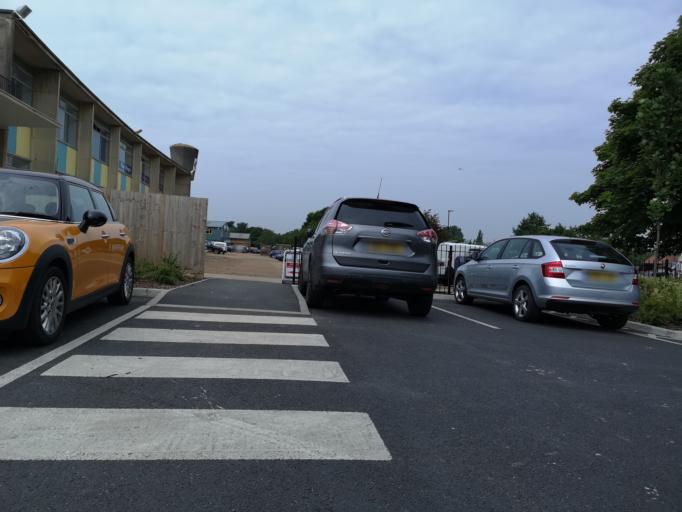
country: GB
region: England
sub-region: Isle of Wight
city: Shanklin
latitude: 50.6457
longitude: -1.1800
